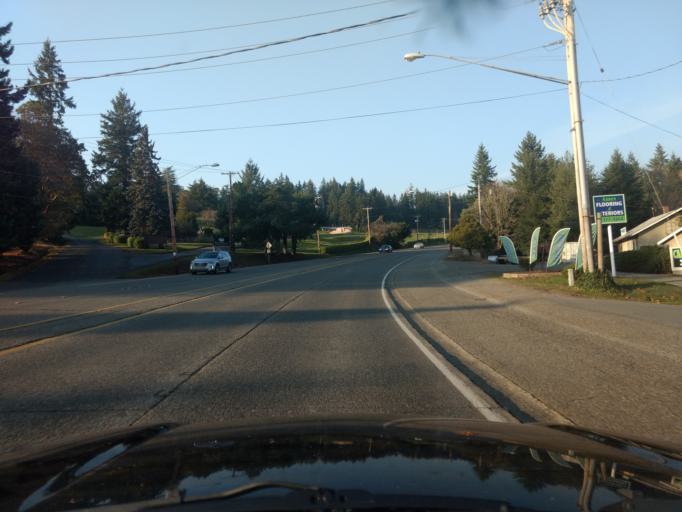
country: US
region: Washington
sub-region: Kitsap County
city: Navy Yard City
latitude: 47.5702
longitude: -122.6867
